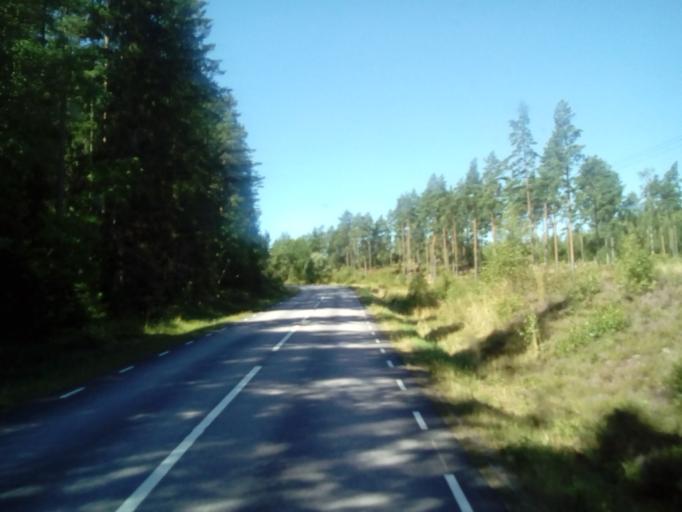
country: SE
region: Kalmar
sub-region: Vasterviks Kommun
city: Overum
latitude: 57.8992
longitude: 16.0686
